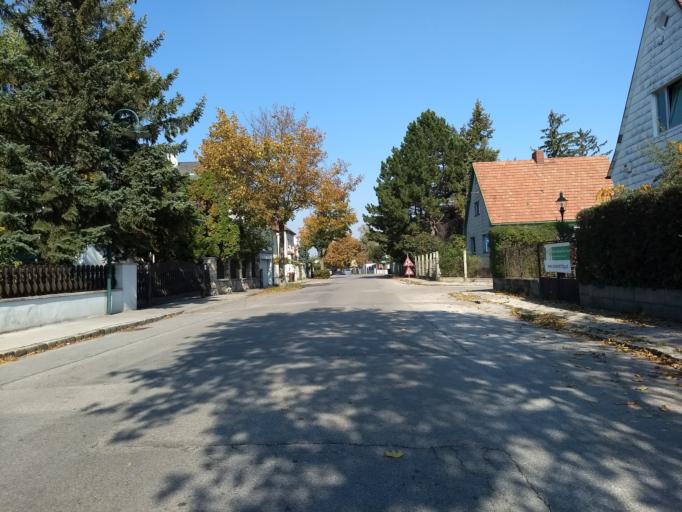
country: AT
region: Lower Austria
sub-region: Politischer Bezirk Modling
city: Brunn am Gebirge
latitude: 48.1104
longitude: 16.2804
